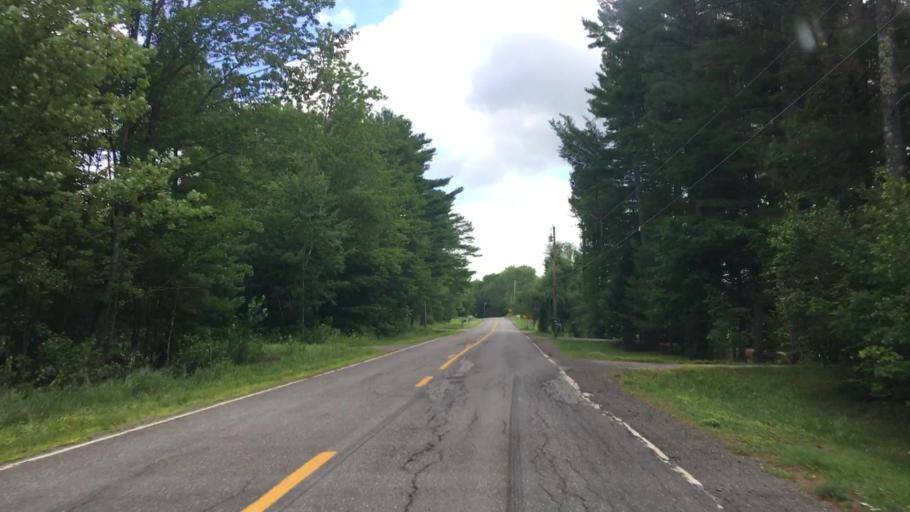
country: US
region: Maine
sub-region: Penobscot County
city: Etna
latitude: 44.7879
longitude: -69.0972
